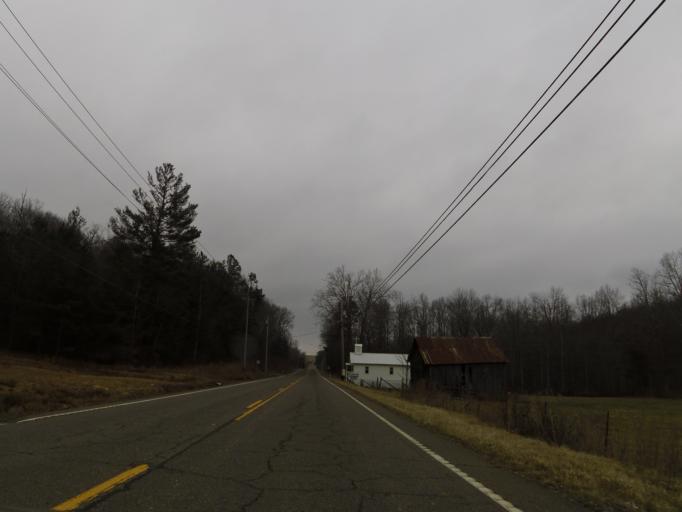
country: US
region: Tennessee
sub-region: Morgan County
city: Wartburg
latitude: 36.2780
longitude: -84.6569
